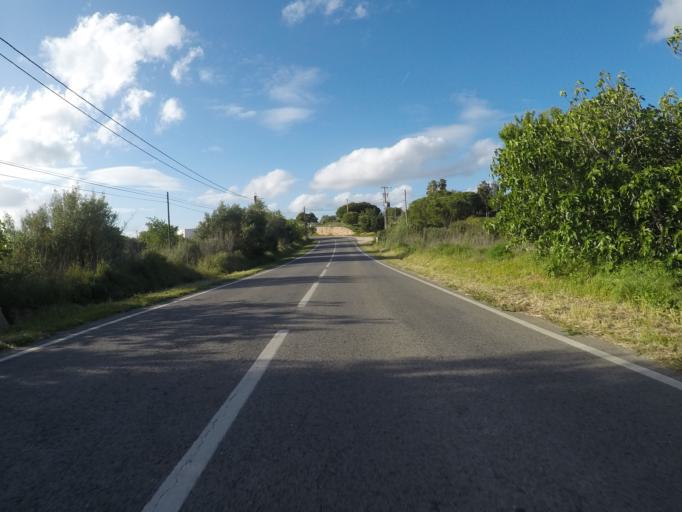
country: PT
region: Faro
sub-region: Lagoa
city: Carvoeiro
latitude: 37.1096
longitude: -8.4459
